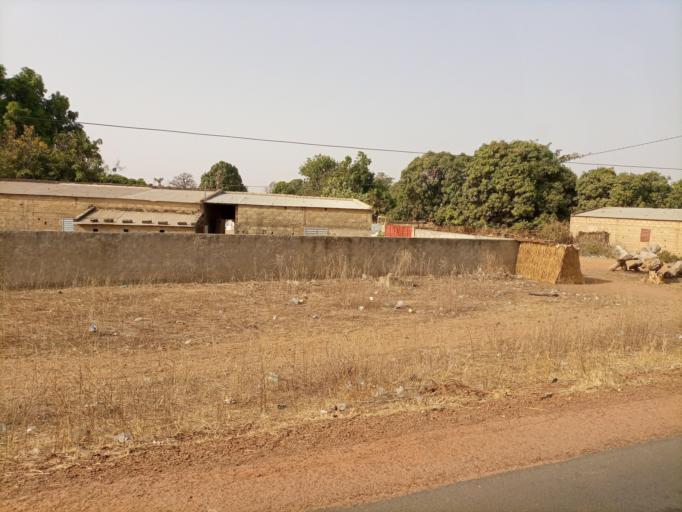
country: SN
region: Fatick
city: Foundiougne
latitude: 14.1208
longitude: -16.4403
